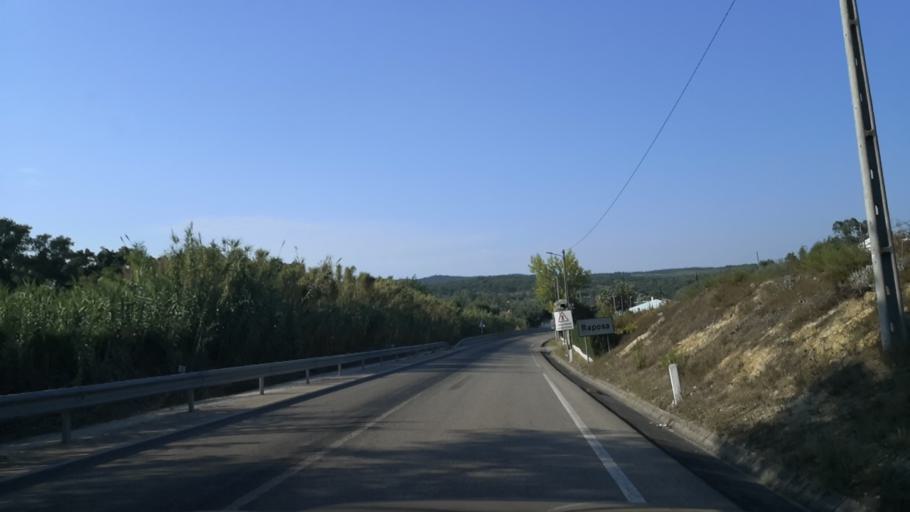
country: PT
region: Santarem
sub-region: Almeirim
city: Fazendas de Almeirim
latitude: 39.1067
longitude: -8.5805
